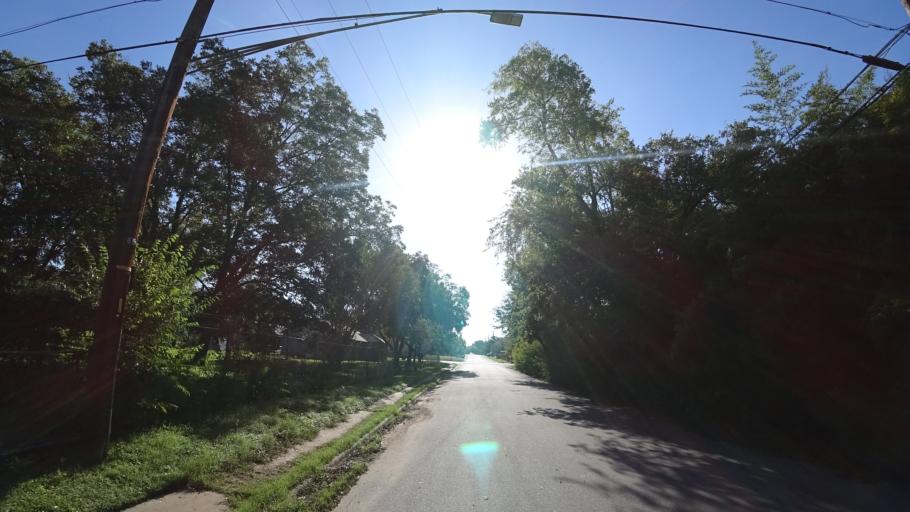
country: US
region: Texas
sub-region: Travis County
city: Wells Branch
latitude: 30.3560
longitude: -97.6971
